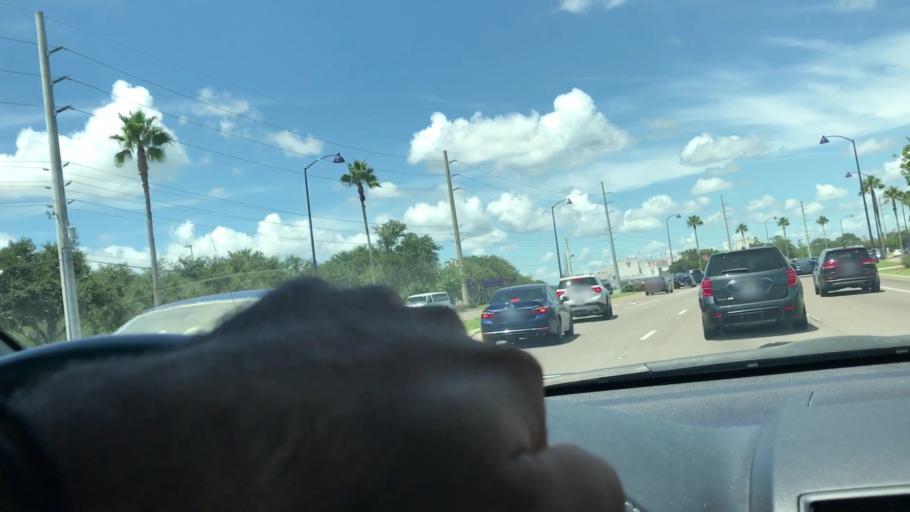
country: US
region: Florida
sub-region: Osceola County
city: Kissimmee
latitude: 28.3040
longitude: -81.4592
